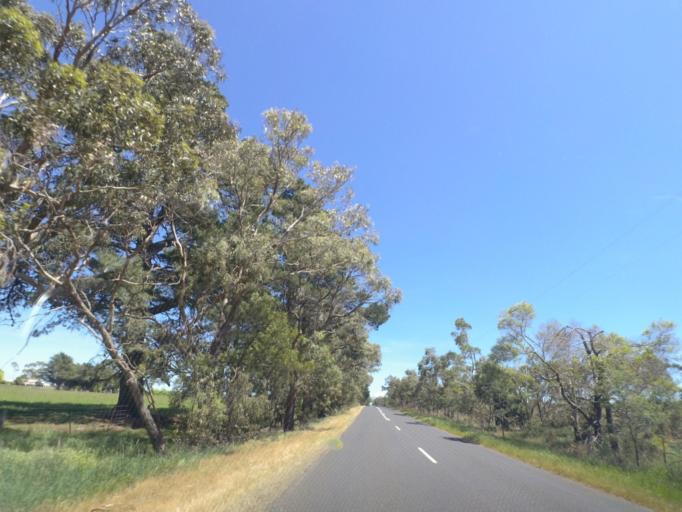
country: AU
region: Victoria
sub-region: Hume
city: Sunbury
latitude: -37.5387
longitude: 144.5969
